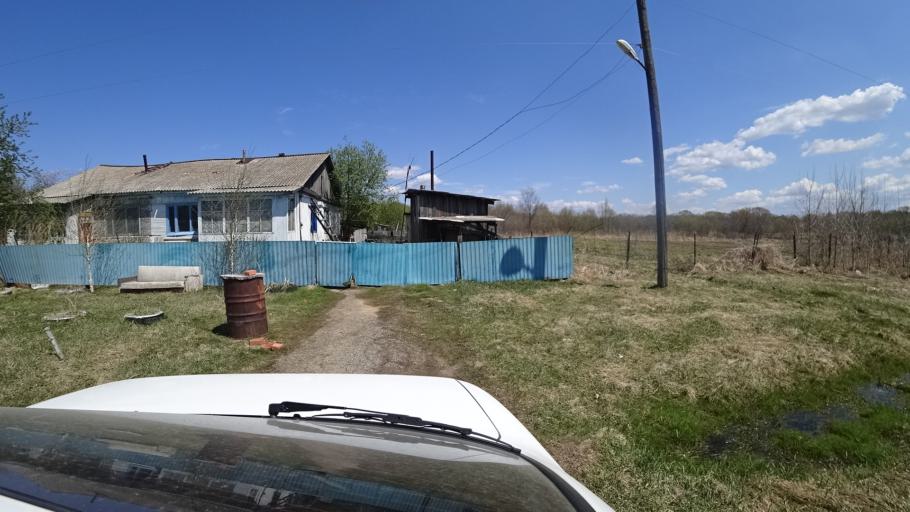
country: RU
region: Primorskiy
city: Lazo
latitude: 45.7900
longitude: 133.7682
